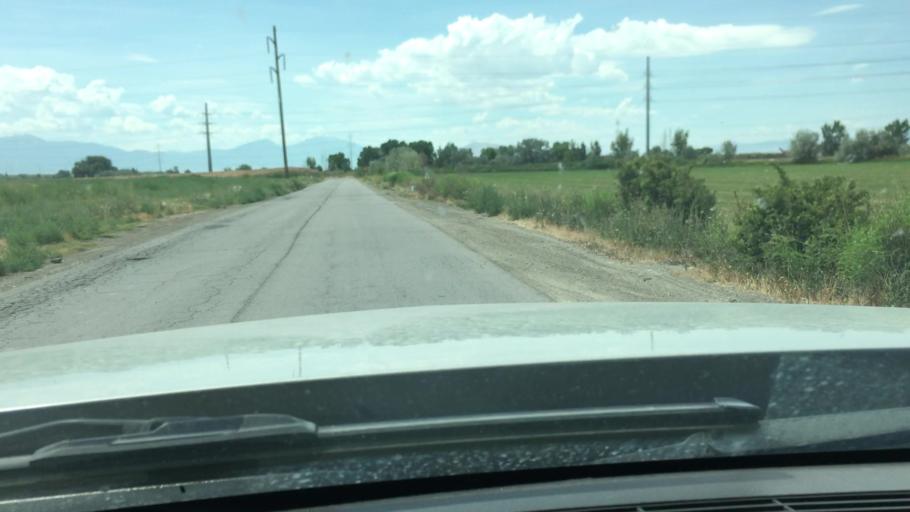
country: US
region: Utah
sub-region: Utah County
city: American Fork
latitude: 40.3469
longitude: -111.7744
